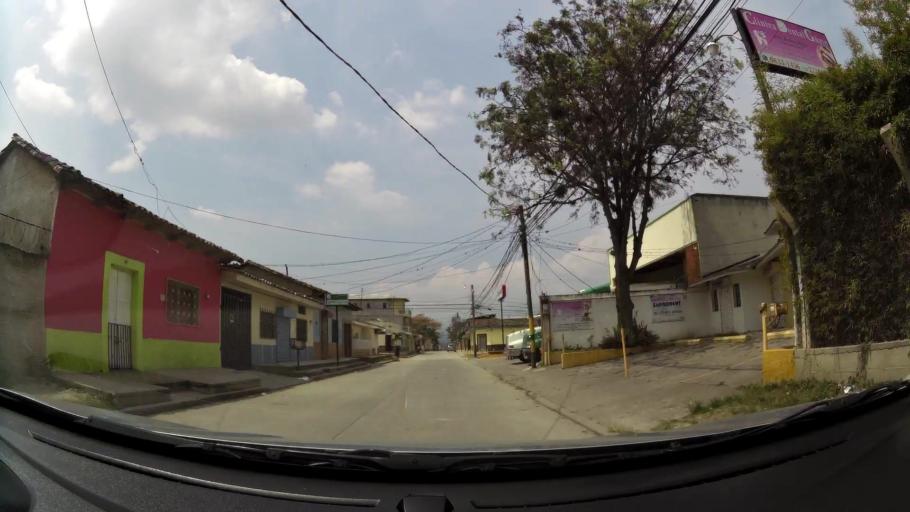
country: HN
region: Comayagua
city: Siguatepeque
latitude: 14.6012
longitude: -87.8302
